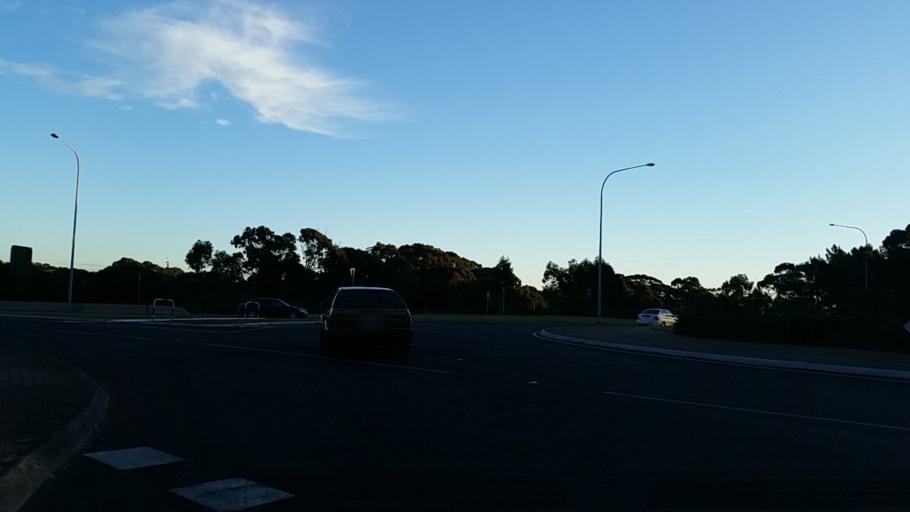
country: AU
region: South Australia
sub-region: Onkaparinga
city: Bedford Park
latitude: -35.0513
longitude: 138.5737
